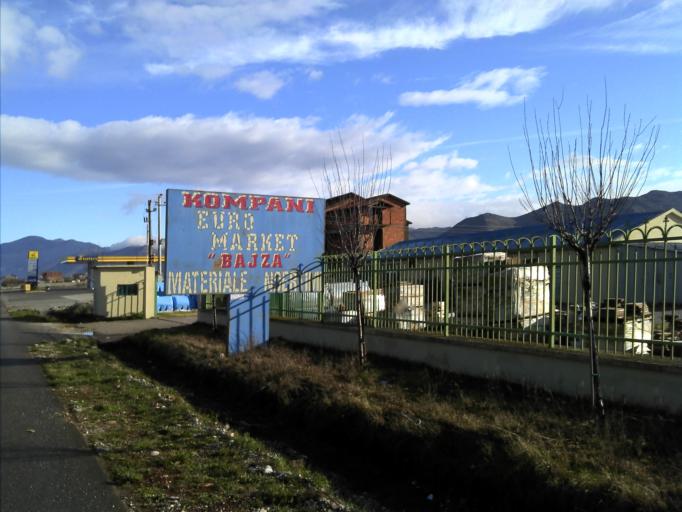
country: AL
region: Shkoder
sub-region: Rrethi i Malesia e Madhe
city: Koplik
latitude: 42.2520
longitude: 19.4265
